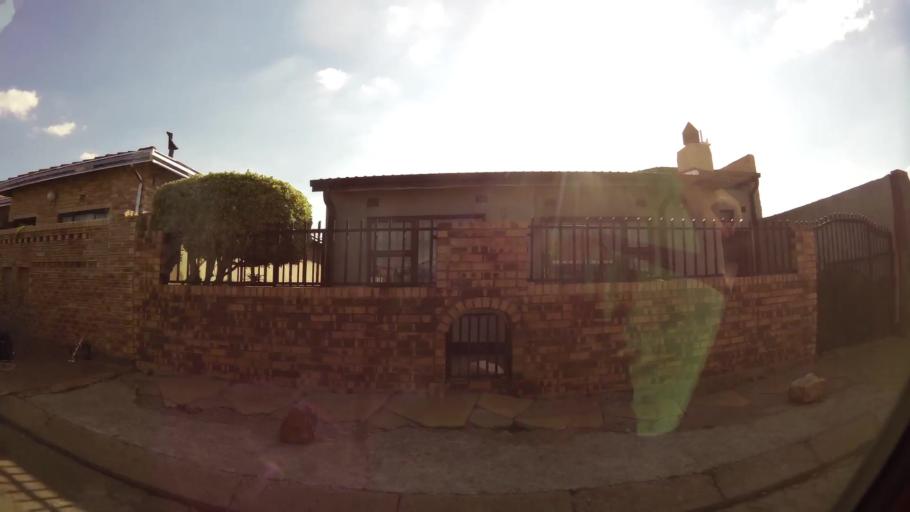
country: ZA
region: Gauteng
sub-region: City of Johannesburg Metropolitan Municipality
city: Soweto
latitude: -26.2282
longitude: 27.8774
